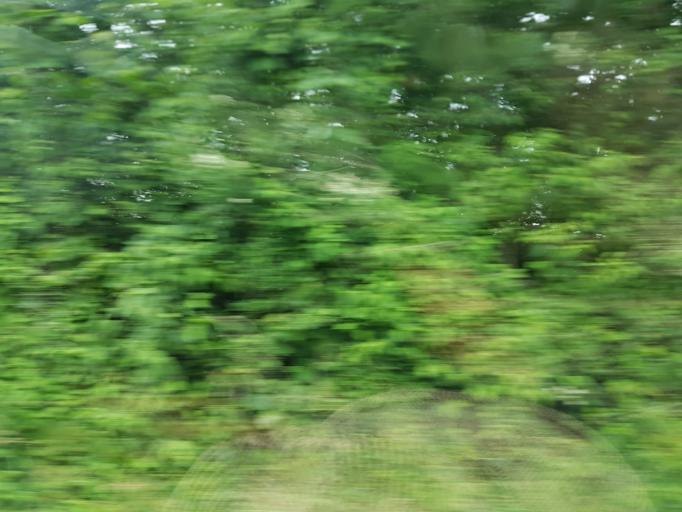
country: FR
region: Bourgogne
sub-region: Departement de la Nievre
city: Corbigny
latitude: 47.1861
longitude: 3.7353
